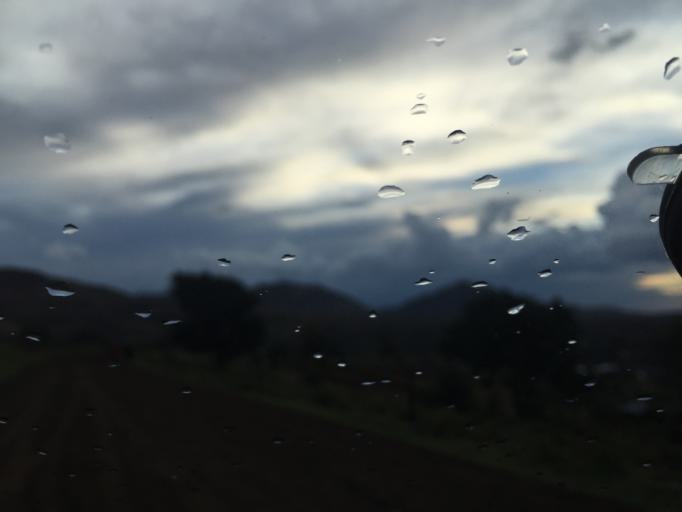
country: LS
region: Leribe
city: Leribe
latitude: -29.1572
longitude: 28.0348
